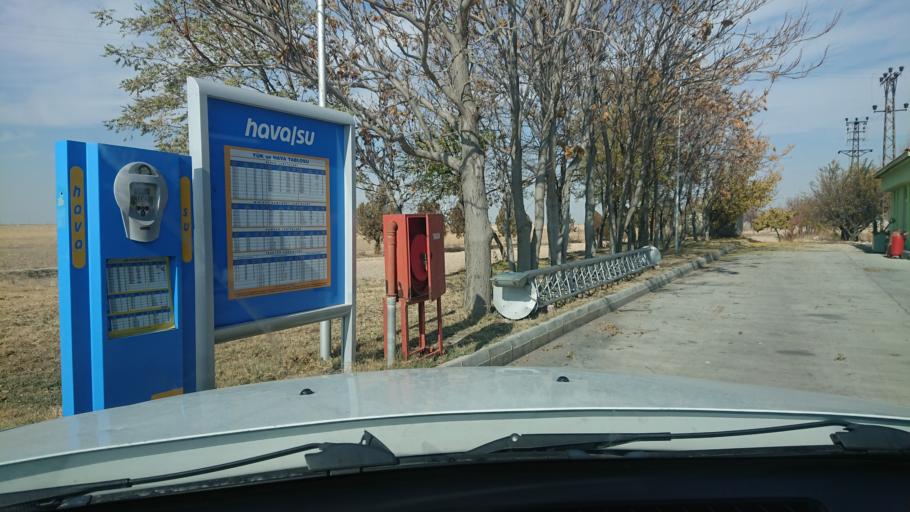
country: TR
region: Aksaray
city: Sultanhani
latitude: 38.2529
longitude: 33.5041
